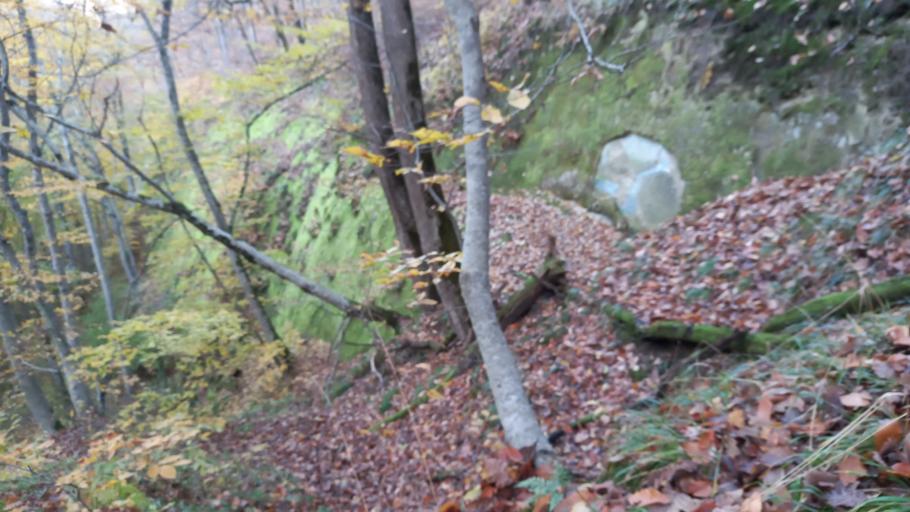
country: RU
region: Krasnodarskiy
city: Goryachiy Klyuch
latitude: 44.6131
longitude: 39.1021
